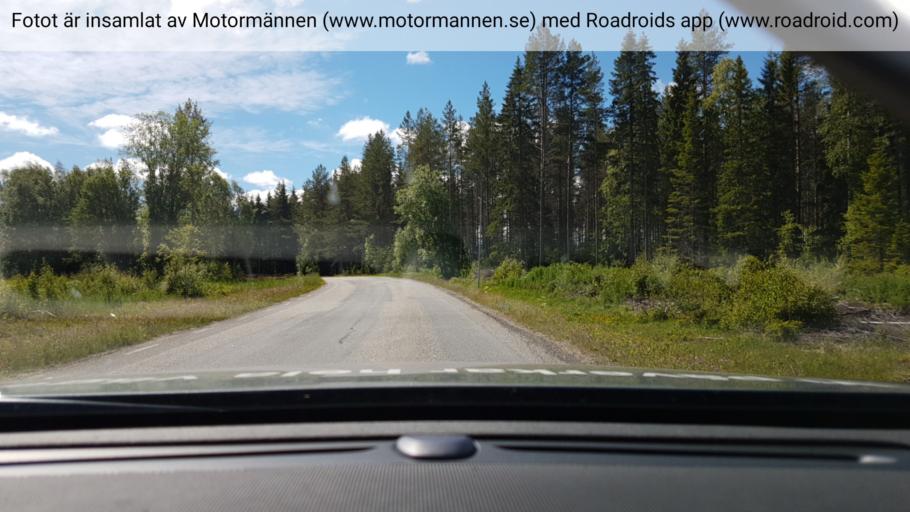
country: SE
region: Vaesterbotten
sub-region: Skelleftea Kommun
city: Burea
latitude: 64.4508
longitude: 21.3543
